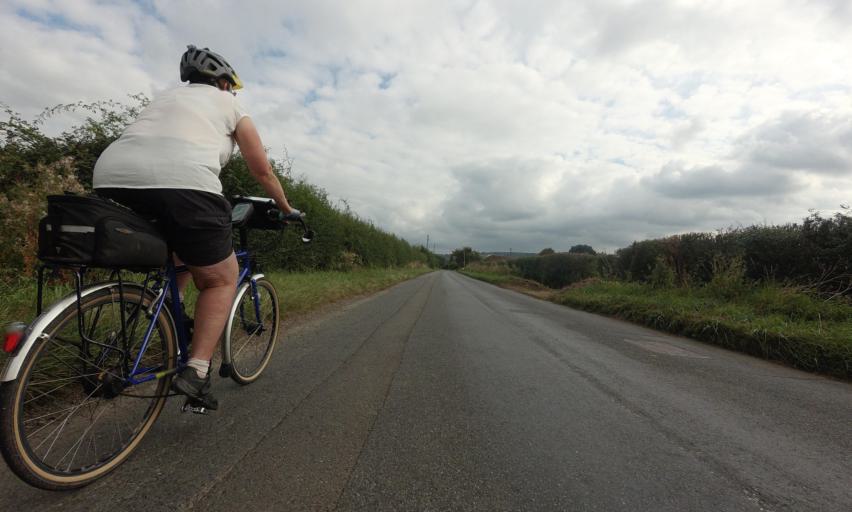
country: GB
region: England
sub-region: Gloucestershire
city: Winchcombe
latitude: 51.9905
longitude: -2.0015
